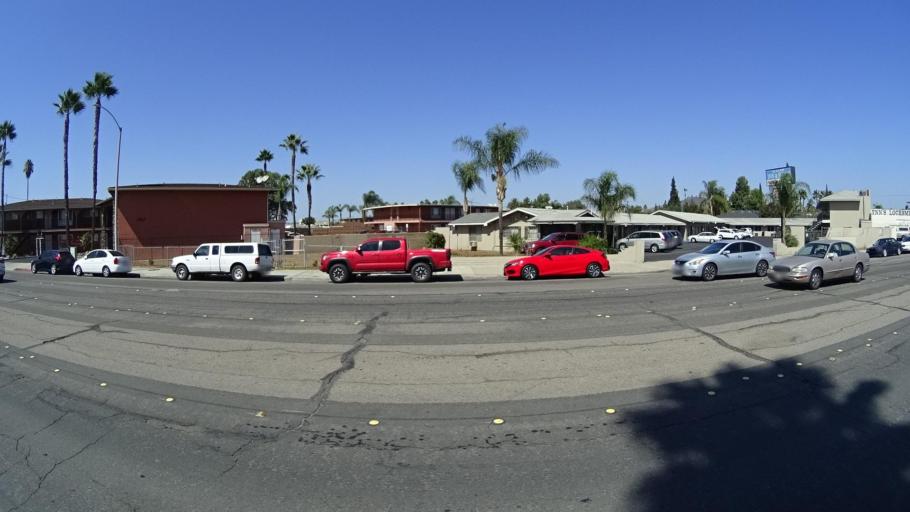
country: US
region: California
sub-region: San Diego County
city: Bostonia
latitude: 32.7986
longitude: -116.9319
